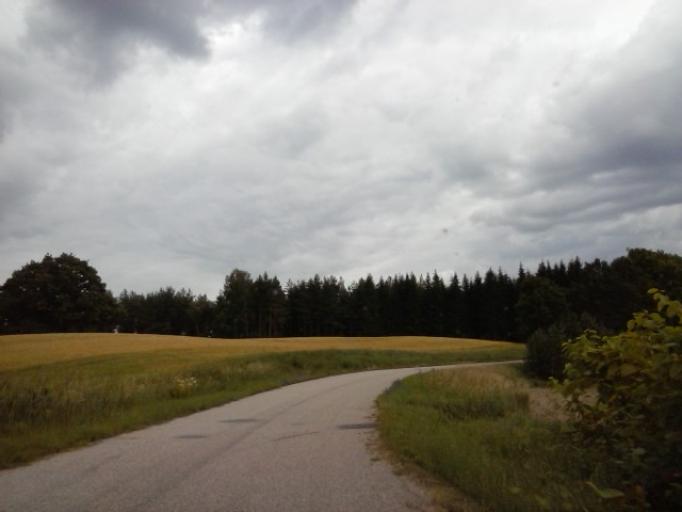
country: EE
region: Vorumaa
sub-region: Voru linn
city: Voru
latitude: 57.7460
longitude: 27.1174
